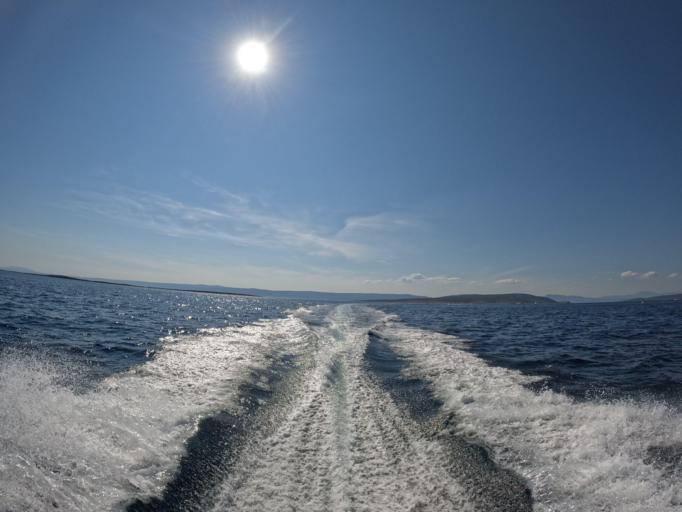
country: HR
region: Primorsko-Goranska
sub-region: Grad Krk
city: Krk
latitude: 44.9541
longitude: 14.5853
